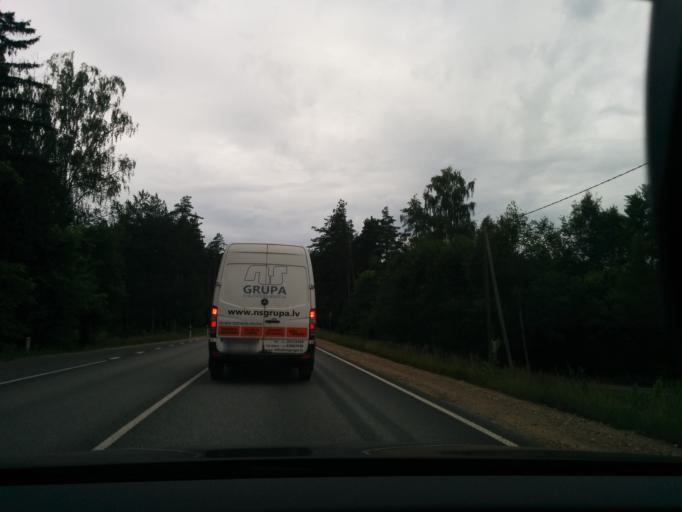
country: LV
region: Salaspils
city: Salaspils
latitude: 56.9039
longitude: 24.3936
